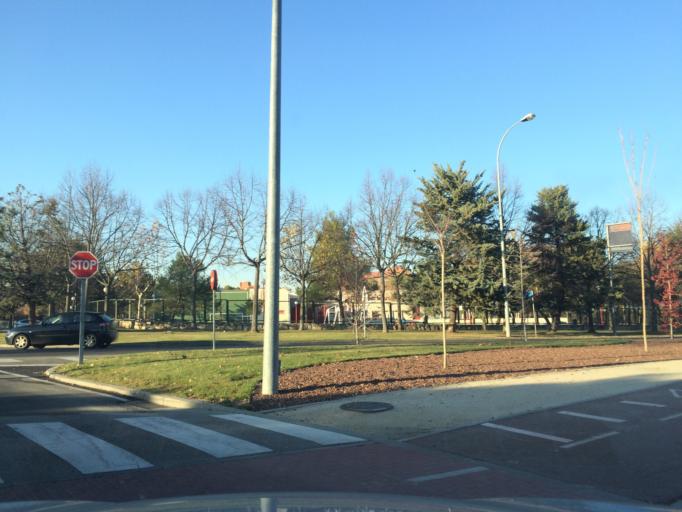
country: ES
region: Madrid
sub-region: Provincia de Madrid
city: Tres Cantos
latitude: 40.5910
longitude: -3.7020
